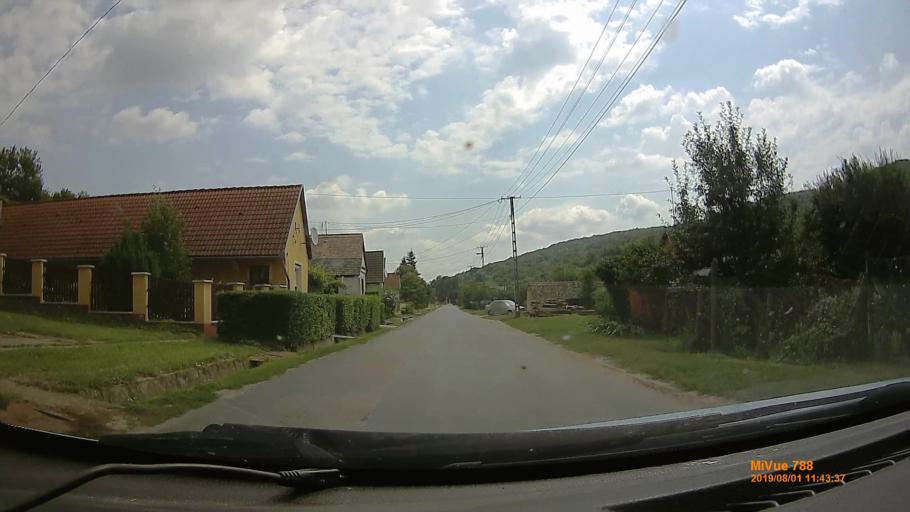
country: HU
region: Baranya
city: Villany
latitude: 45.8811
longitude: 18.4215
